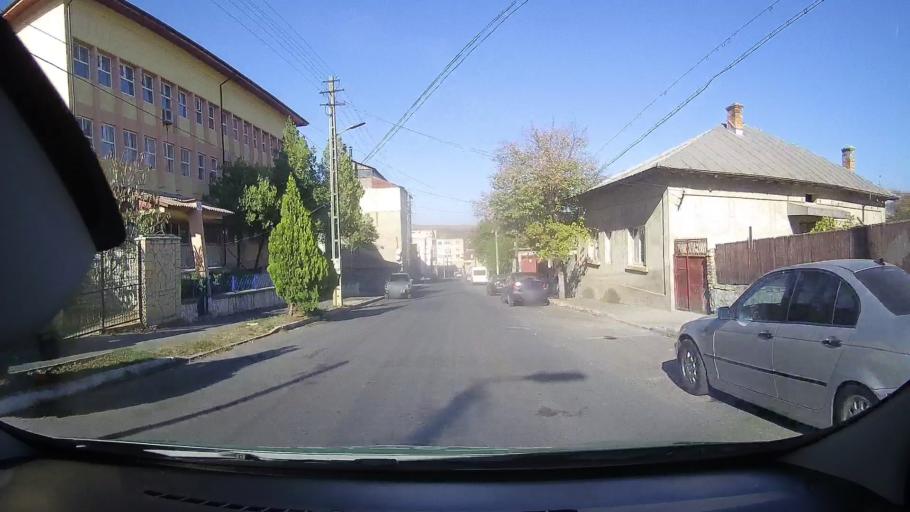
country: RO
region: Tulcea
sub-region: Oras Babadag
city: Babadag
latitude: 44.8927
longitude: 28.7260
